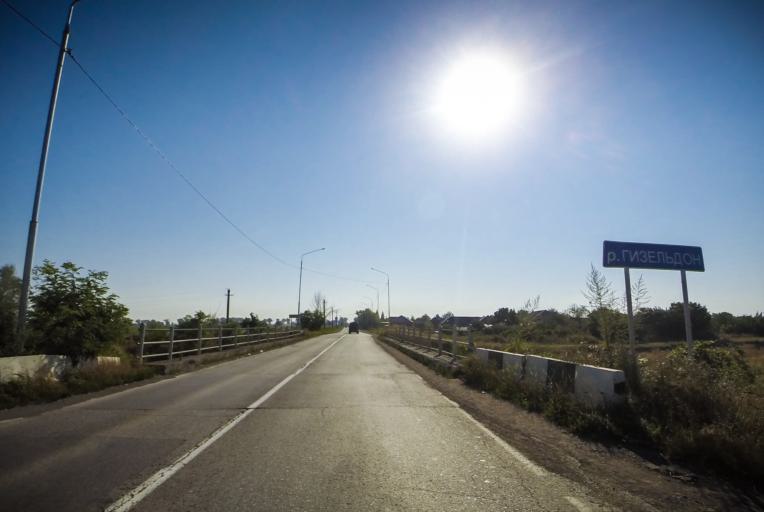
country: RU
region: North Ossetia
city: Arkhonskaya
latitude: 43.1174
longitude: 44.4997
